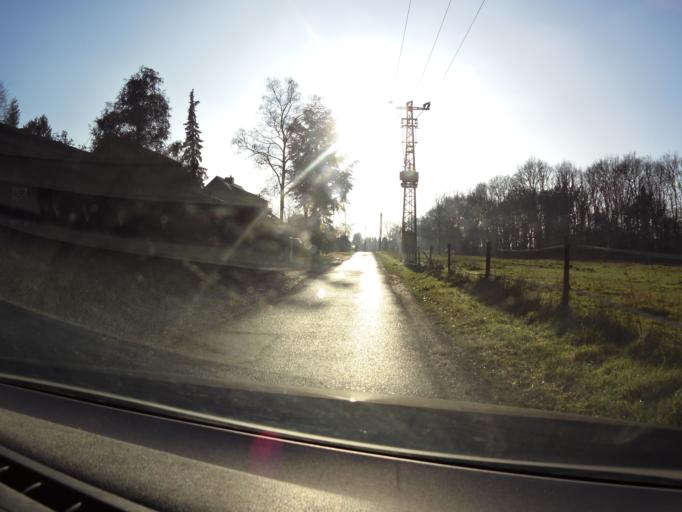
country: DE
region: North Rhine-Westphalia
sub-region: Regierungsbezirk Dusseldorf
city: Nettetal
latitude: 51.3419
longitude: 6.2603
